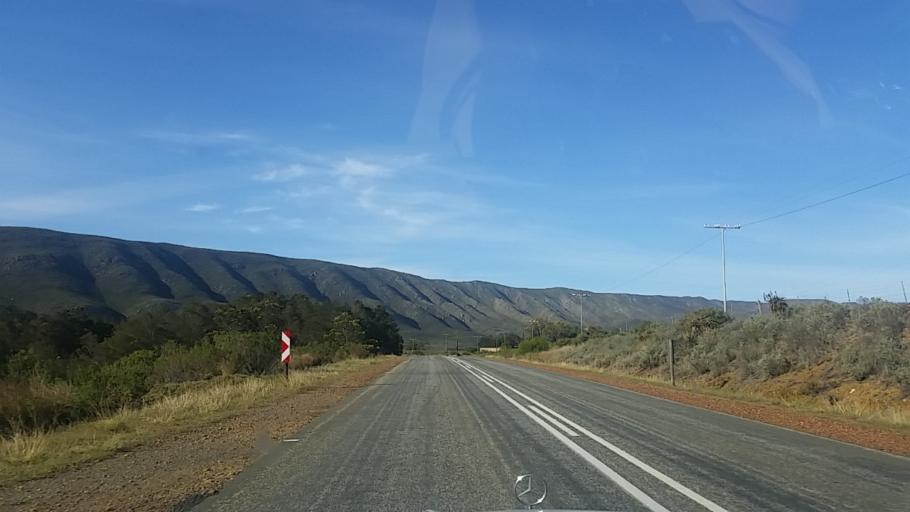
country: ZA
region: Western Cape
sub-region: Eden District Municipality
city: Knysna
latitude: -33.7727
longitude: 22.9596
